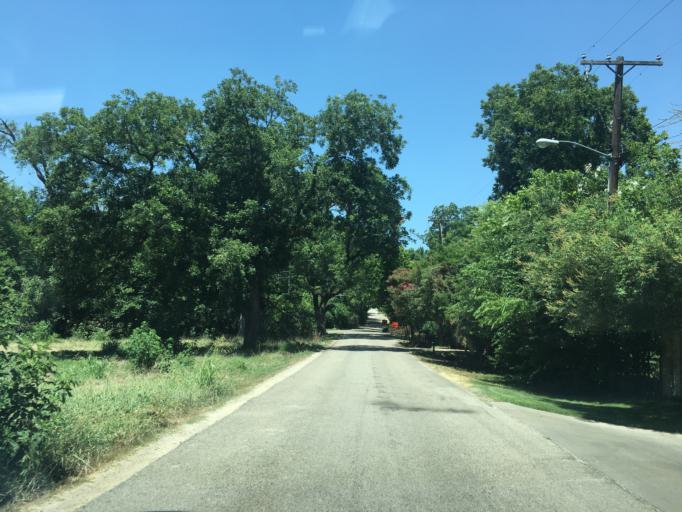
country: US
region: Texas
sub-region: Dallas County
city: Highland Park
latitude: 32.8374
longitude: -96.7309
